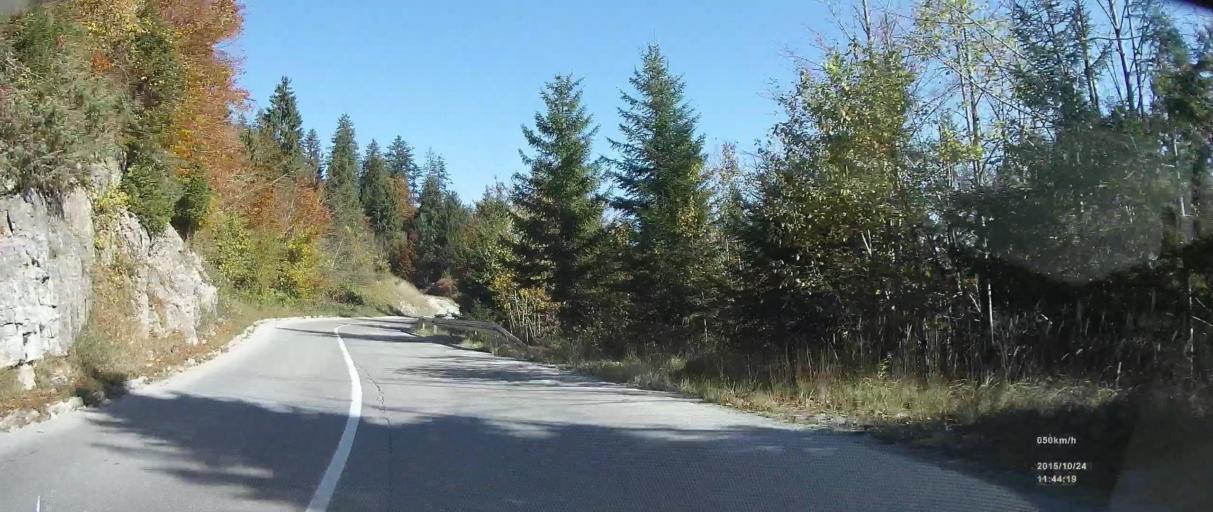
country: SI
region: Osilnica
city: Osilnica
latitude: 45.4391
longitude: 14.7087
